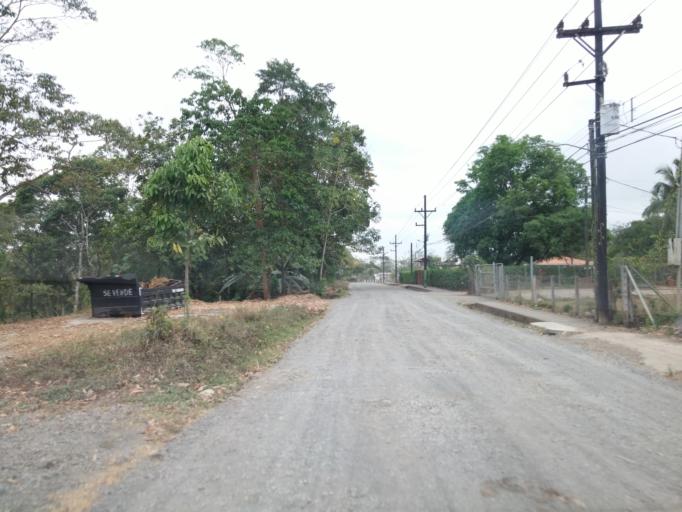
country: CR
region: Alajuela
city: Quesada
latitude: 10.3146
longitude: -84.5226
